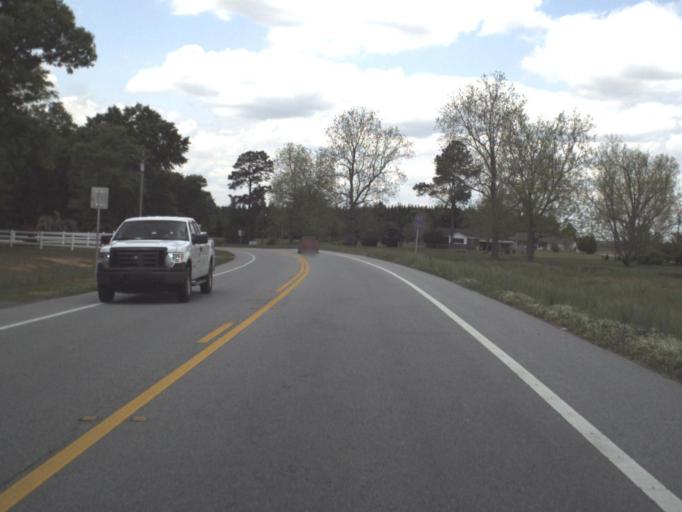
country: US
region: Alabama
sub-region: Escambia County
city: Atmore
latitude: 30.9215
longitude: -87.4801
